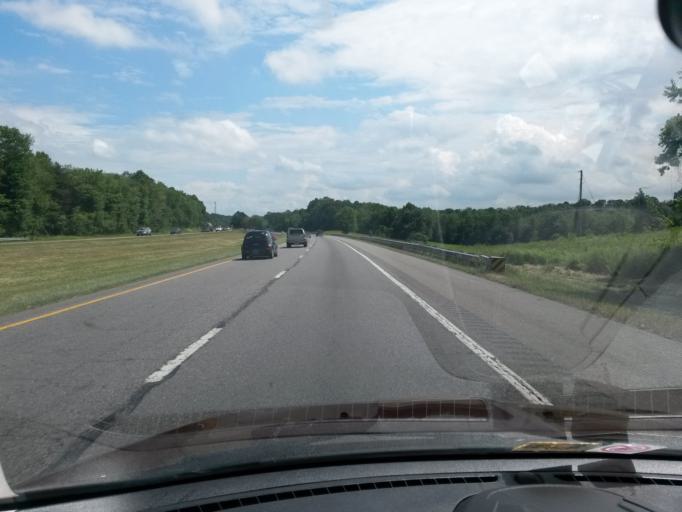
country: US
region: North Carolina
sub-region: Surry County
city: Dobson
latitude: 36.3563
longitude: -80.7987
